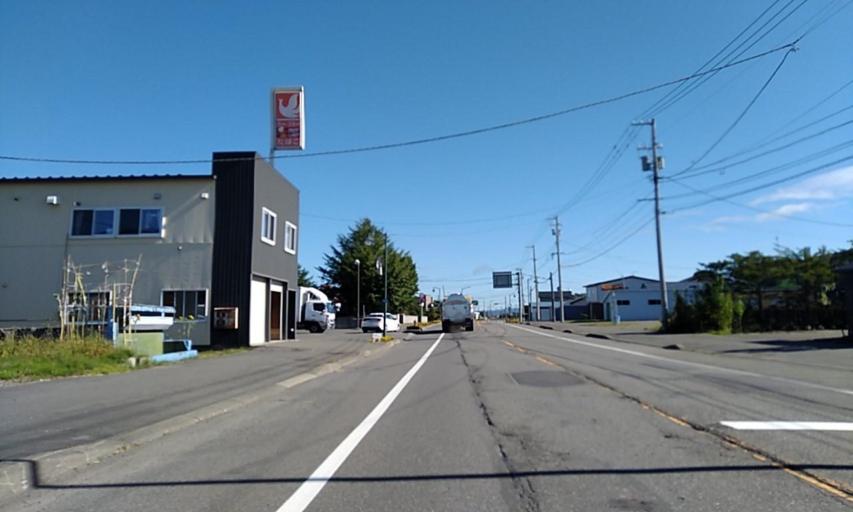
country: JP
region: Hokkaido
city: Shizunai-furukawacho
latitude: 42.5202
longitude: 142.0339
